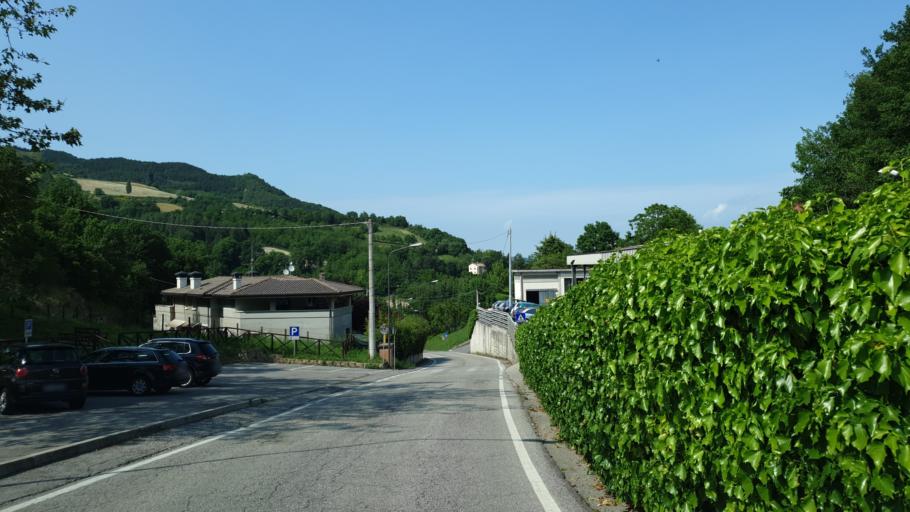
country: IT
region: Emilia-Romagna
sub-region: Forli-Cesena
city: Sarsina
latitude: 43.9216
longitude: 12.1643
